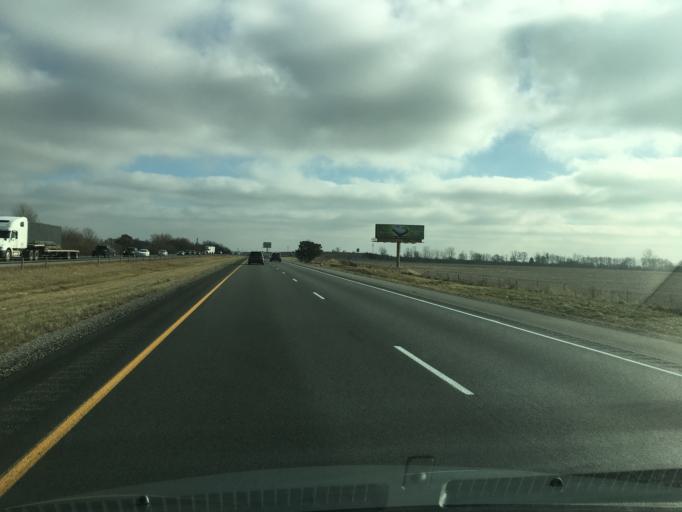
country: US
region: Indiana
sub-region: Clinton County
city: Mulberry
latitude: 40.2713
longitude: -86.6681
